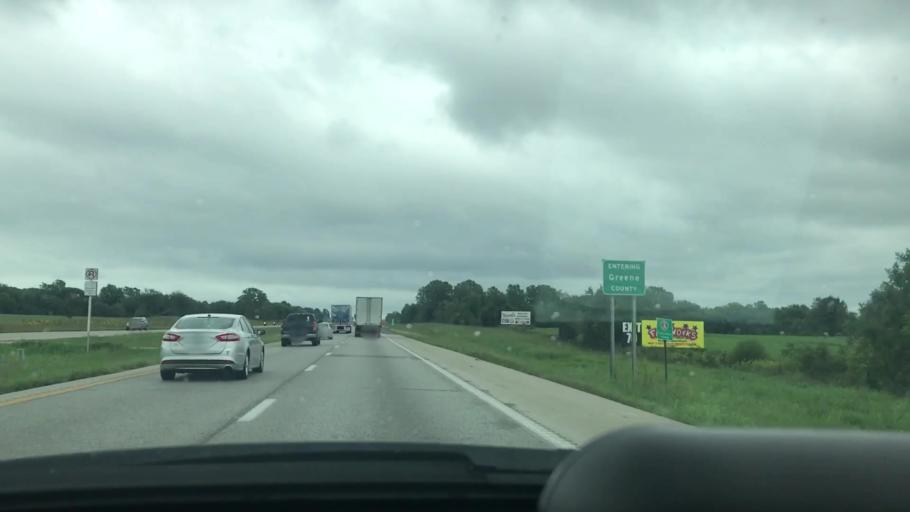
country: US
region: Missouri
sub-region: Greene County
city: Ash Grove
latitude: 37.1866
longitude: -93.6074
